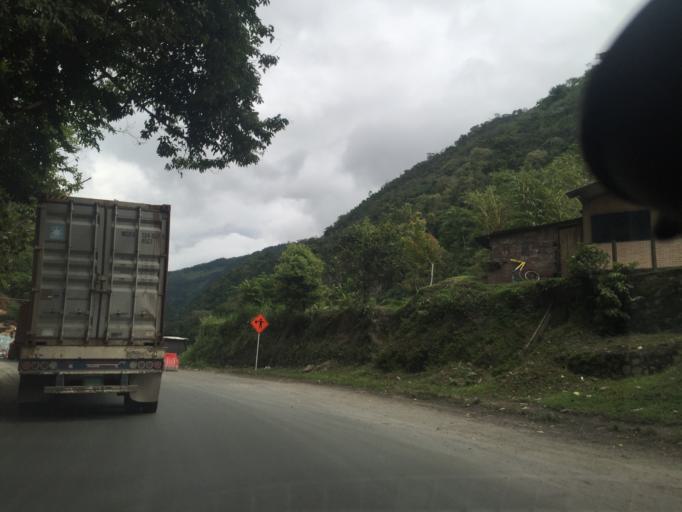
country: CO
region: Valle del Cauca
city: Dagua
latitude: 3.7778
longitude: -76.7579
